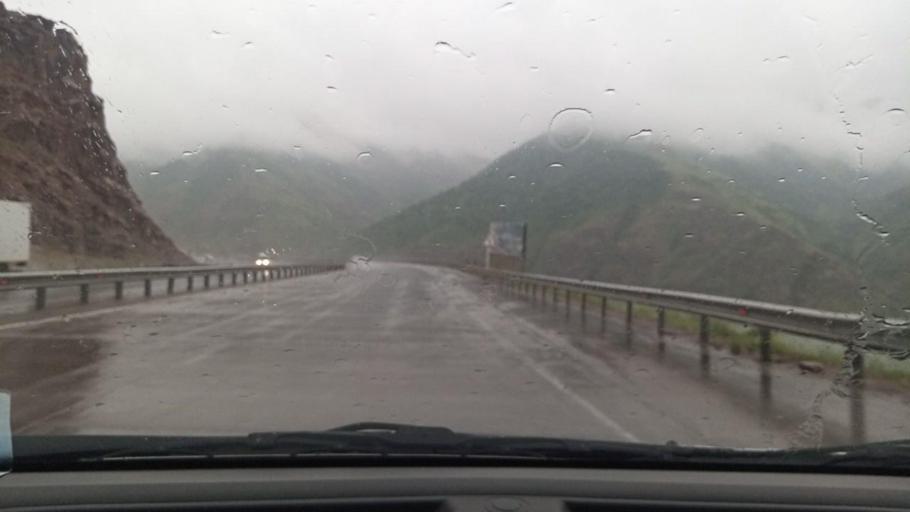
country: UZ
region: Toshkent
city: Angren
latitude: 41.0730
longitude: 70.2693
